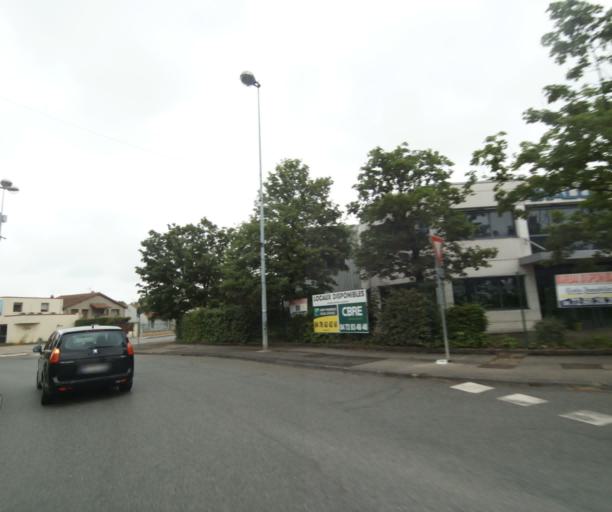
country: FR
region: Rhone-Alpes
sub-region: Departement du Rhone
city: Vaulx-en-Velin
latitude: 45.7884
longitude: 4.9072
